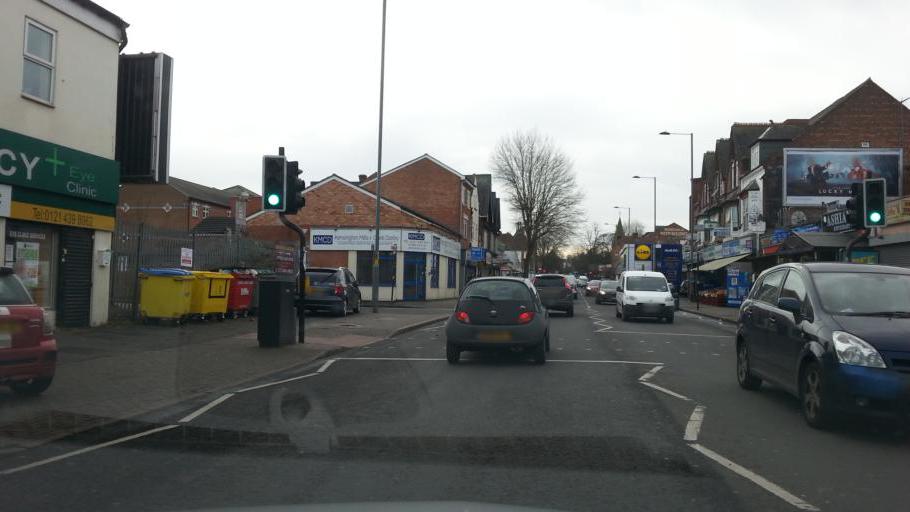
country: GB
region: England
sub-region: City and Borough of Birmingham
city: Birmingham
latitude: 52.4569
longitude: -1.8858
